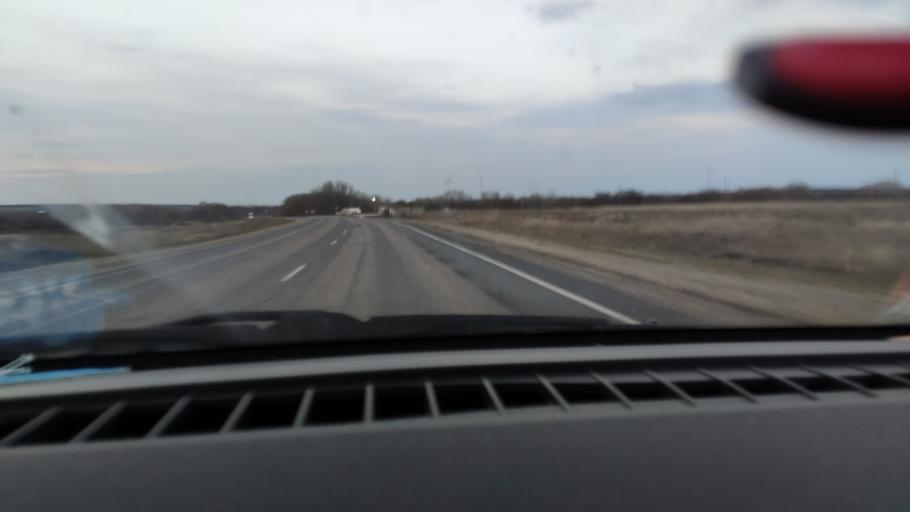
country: RU
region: Saratov
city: Sinodskoye
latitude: 51.9757
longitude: 46.6476
